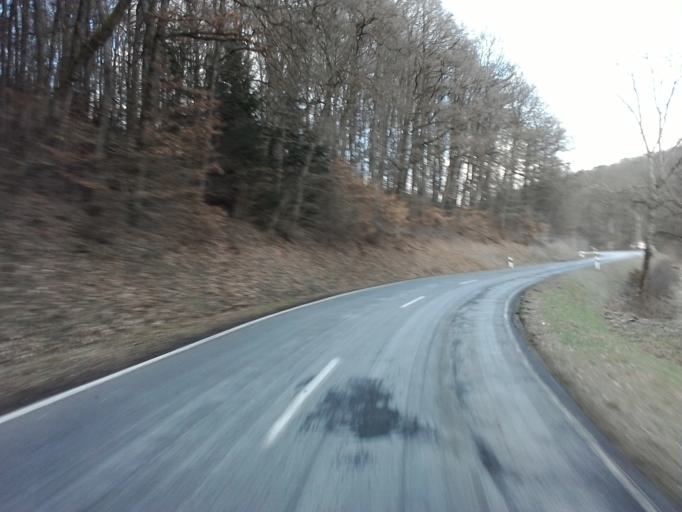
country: DE
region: Rheinland-Pfalz
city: Uppershausen
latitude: 50.0523
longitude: 6.3072
